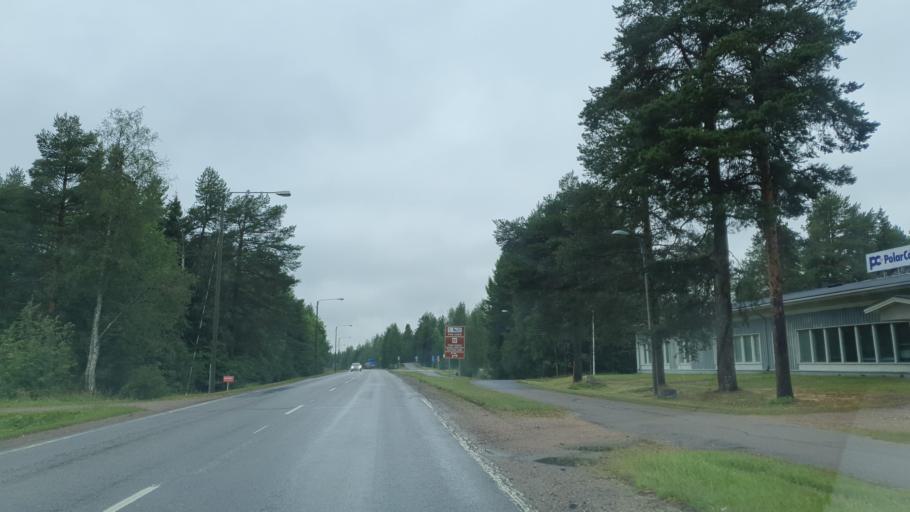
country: FI
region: Lapland
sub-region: Itae-Lappi
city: Kemijaervi
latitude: 66.7193
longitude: 27.3777
